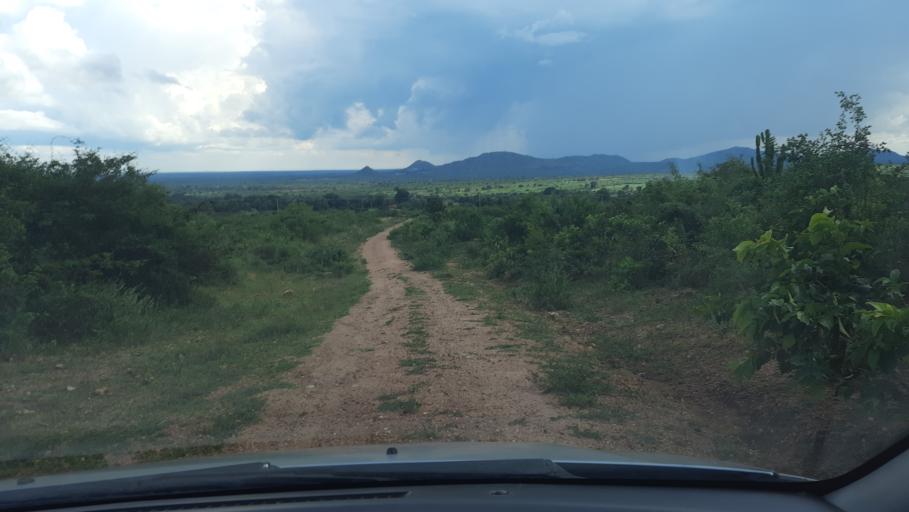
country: UG
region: Central Region
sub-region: Nakasongola District
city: Nakasongola
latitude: 1.3837
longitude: 32.5103
